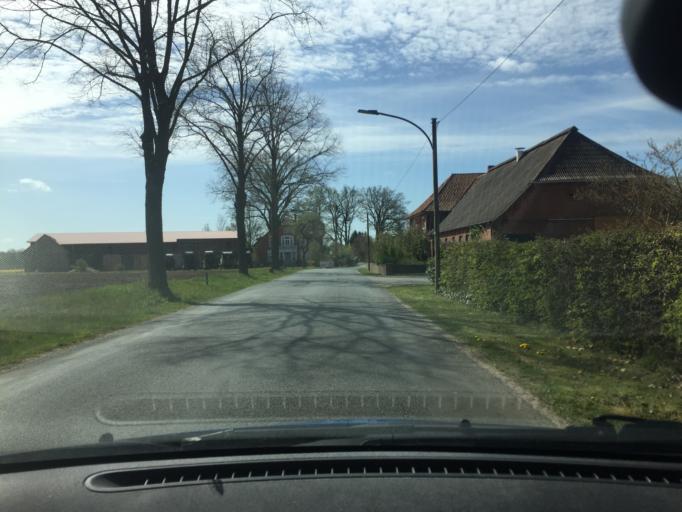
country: DE
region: Lower Saxony
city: Suhlendorf
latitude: 52.9256
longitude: 10.7118
